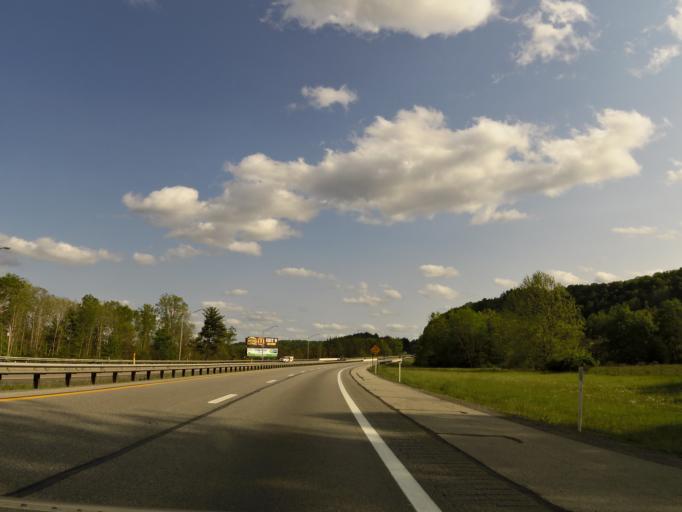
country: US
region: West Virginia
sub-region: Mercer County
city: Athens
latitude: 37.4726
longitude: -81.0679
